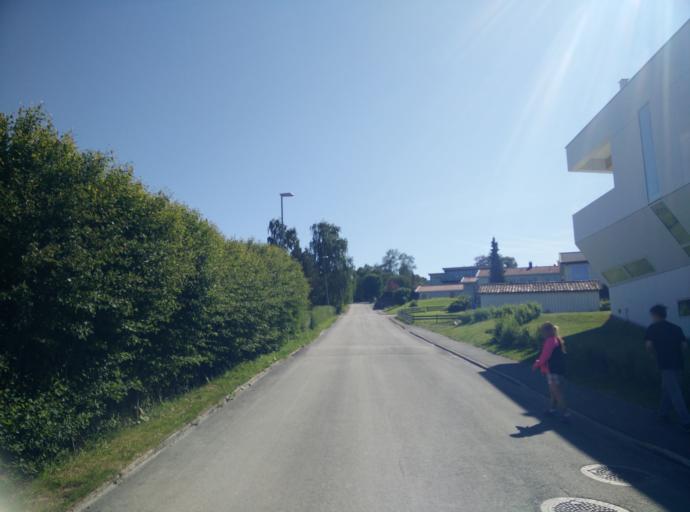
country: NO
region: Sor-Trondelag
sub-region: Trondheim
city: Trondheim
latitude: 63.4105
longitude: 10.3736
